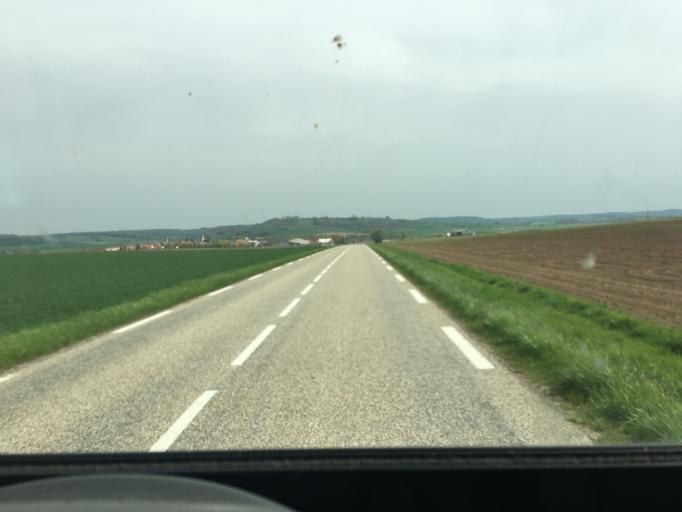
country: FR
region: Lorraine
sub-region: Departement de la Moselle
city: Vic-sur-Seille
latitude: 48.7658
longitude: 6.5581
